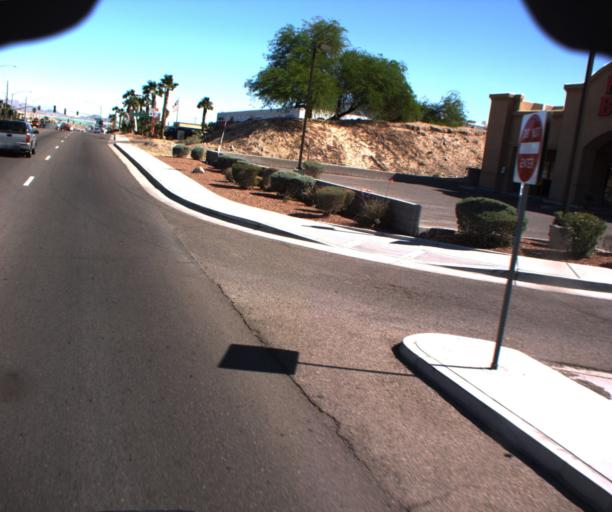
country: US
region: Arizona
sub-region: Mohave County
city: Bullhead City
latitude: 35.1037
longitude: -114.5979
